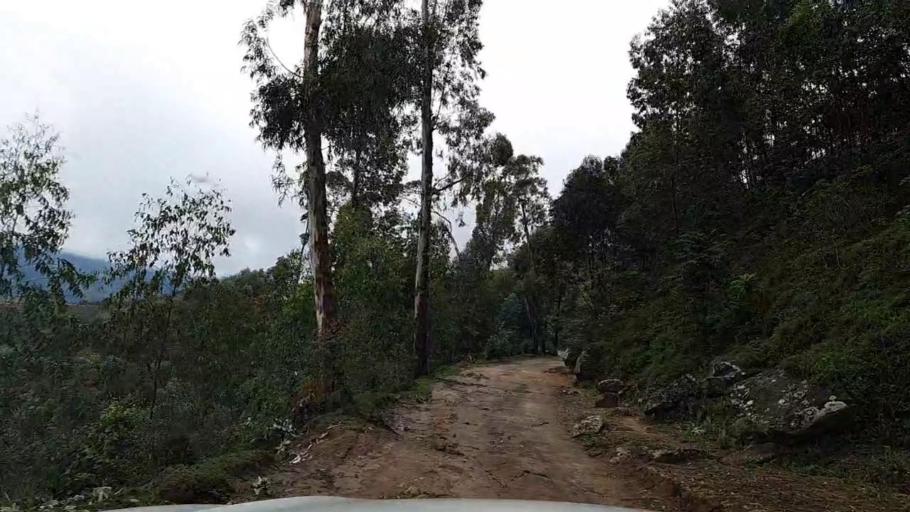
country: RW
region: Southern Province
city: Gikongoro
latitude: -2.3657
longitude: 29.4959
